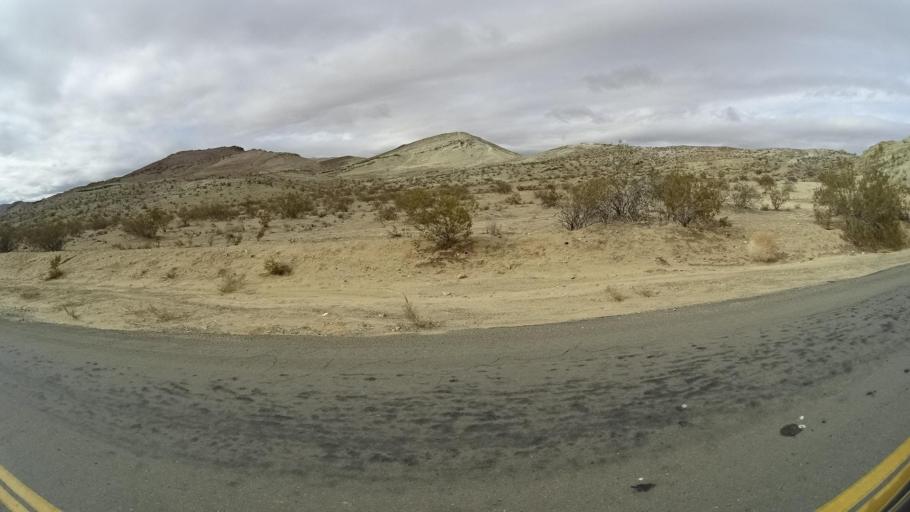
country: US
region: California
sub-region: Kern County
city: Rosamond
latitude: 34.9213
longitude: -118.2134
